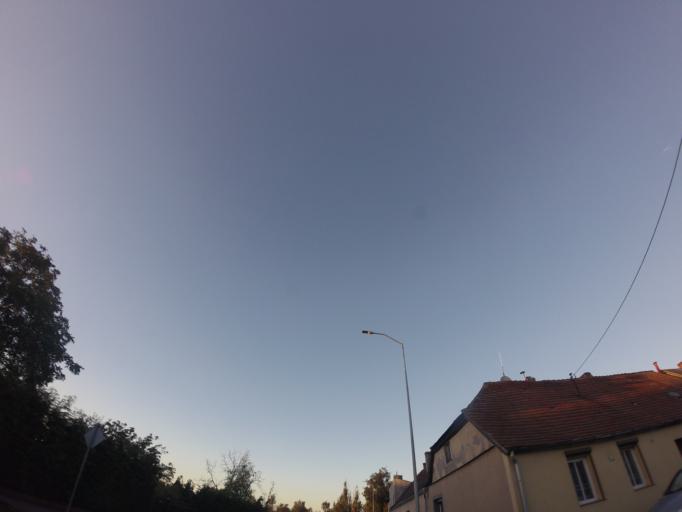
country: PL
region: Lubusz
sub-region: Powiat strzelecko-drezdenecki
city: Drezdenko
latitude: 52.8406
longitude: 15.8353
